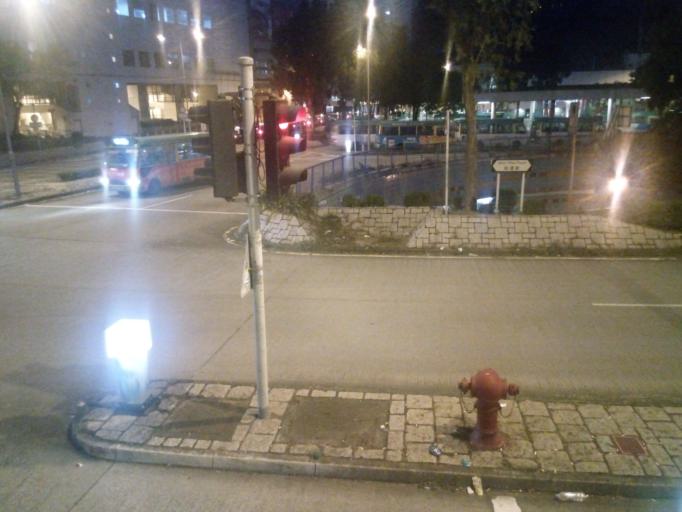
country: HK
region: Tai Po
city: Tai Po
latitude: 22.4431
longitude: 114.1702
